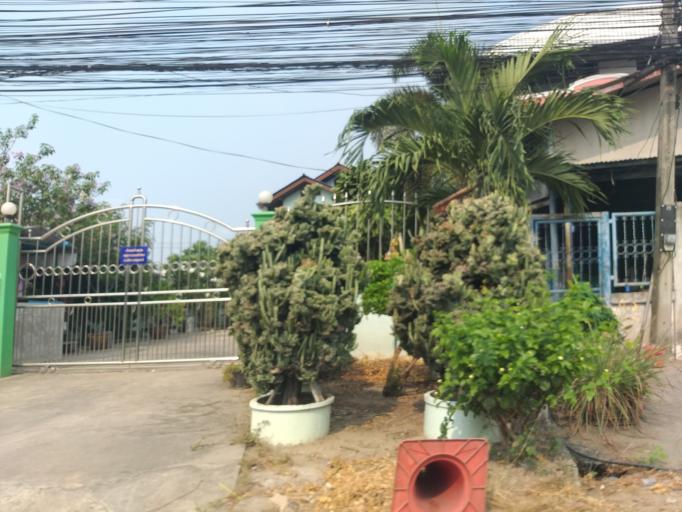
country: TH
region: Phra Nakhon Si Ayutthaya
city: Ban Bang Kadi Pathum Thani
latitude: 14.0249
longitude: 100.5644
